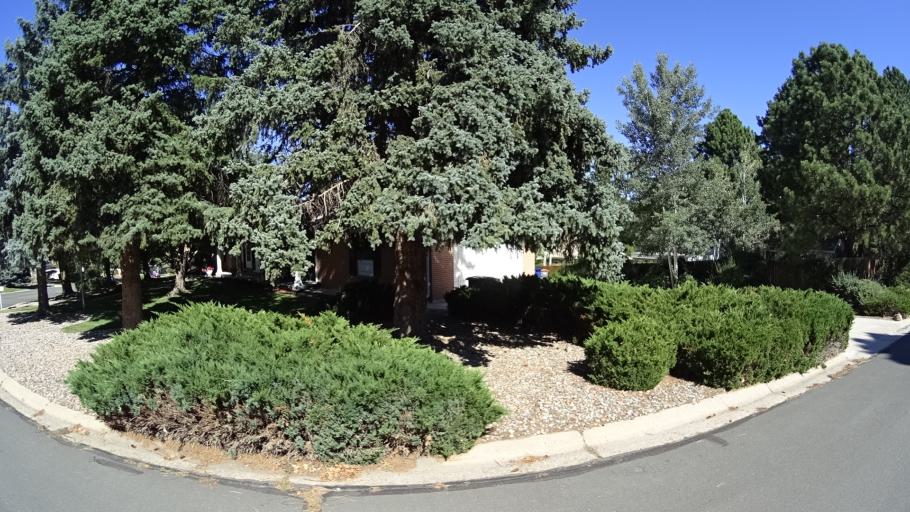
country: US
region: Colorado
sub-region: El Paso County
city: Colorado Springs
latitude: 38.8753
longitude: -104.7794
